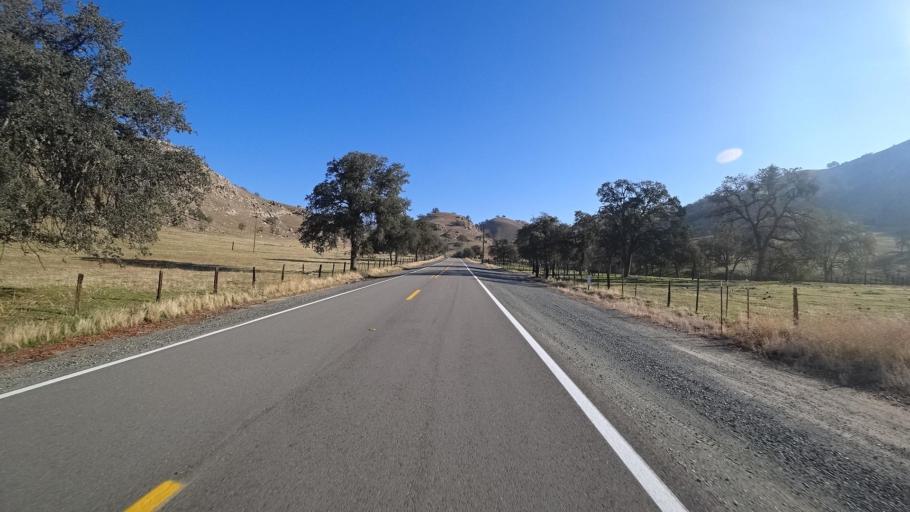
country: US
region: California
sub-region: Kern County
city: Alta Sierra
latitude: 35.7062
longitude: -118.8297
